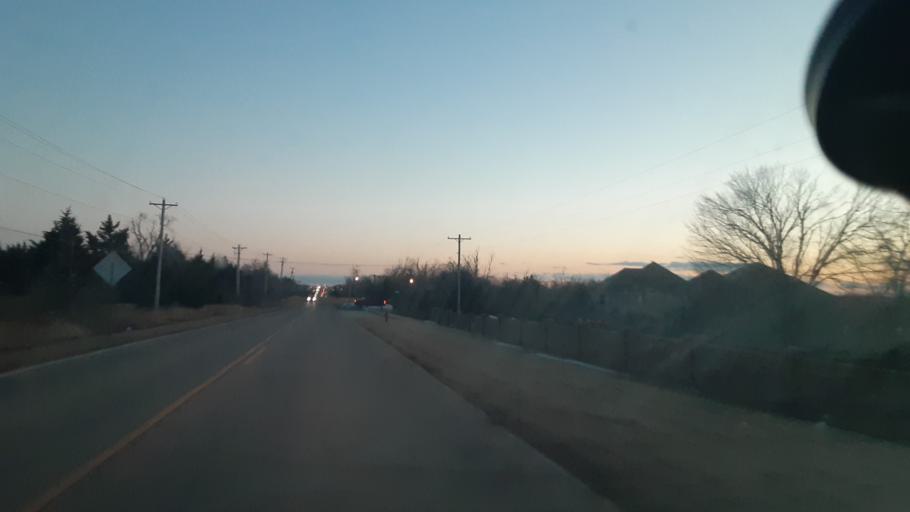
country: US
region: Oklahoma
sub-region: Oklahoma County
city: Edmond
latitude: 35.6610
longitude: -97.4251
